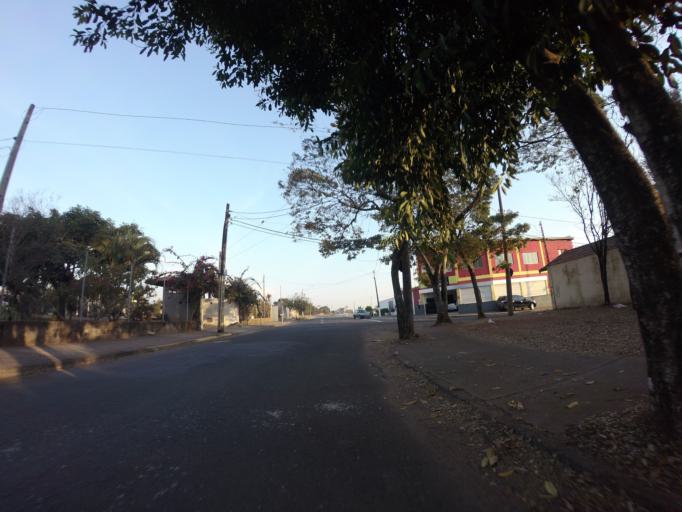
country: BR
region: Sao Paulo
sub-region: Piracicaba
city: Piracicaba
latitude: -22.7663
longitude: -47.5928
